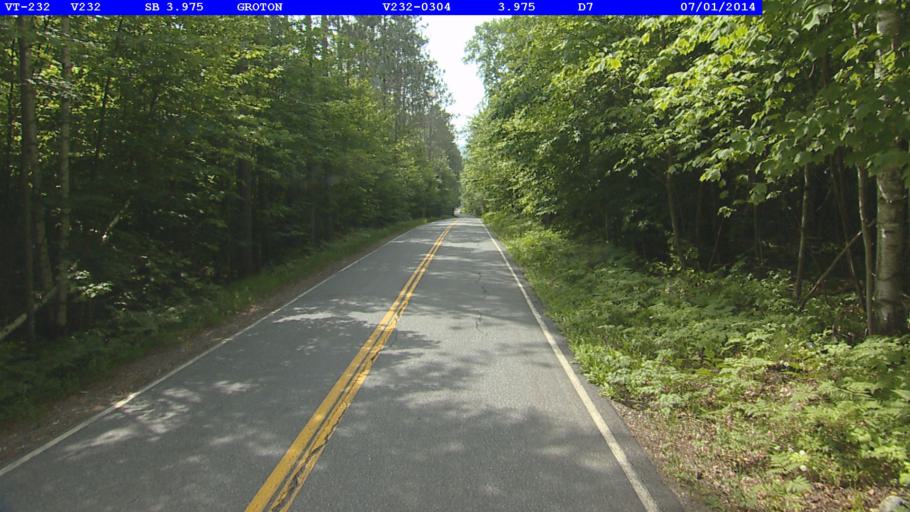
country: US
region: Vermont
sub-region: Washington County
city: Barre
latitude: 44.2603
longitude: -72.2715
